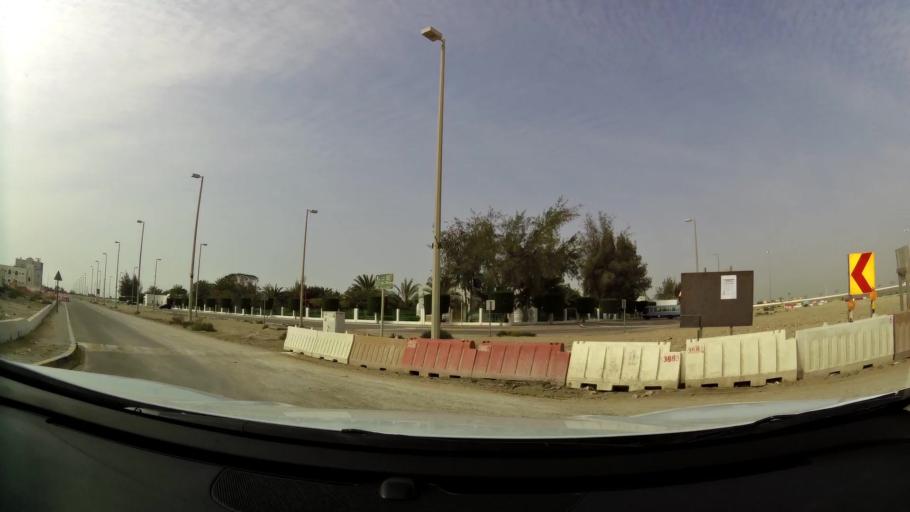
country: AE
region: Abu Dhabi
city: Abu Dhabi
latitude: 24.6202
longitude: 54.7127
